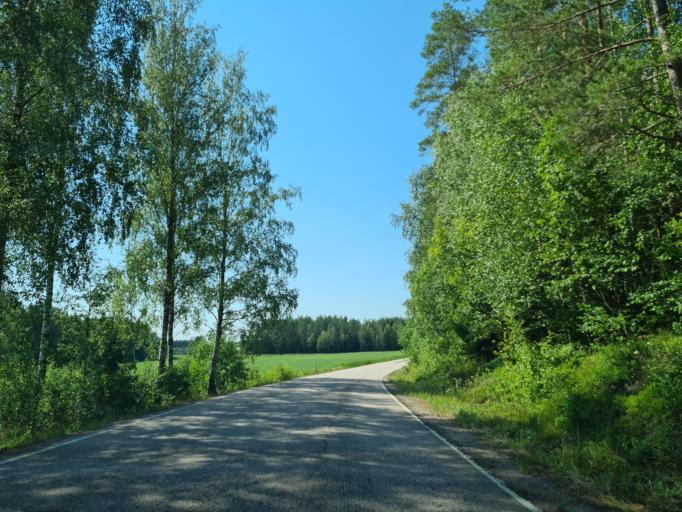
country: FI
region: Varsinais-Suomi
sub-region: Loimaa
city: Aura
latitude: 60.6031
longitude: 22.6011
